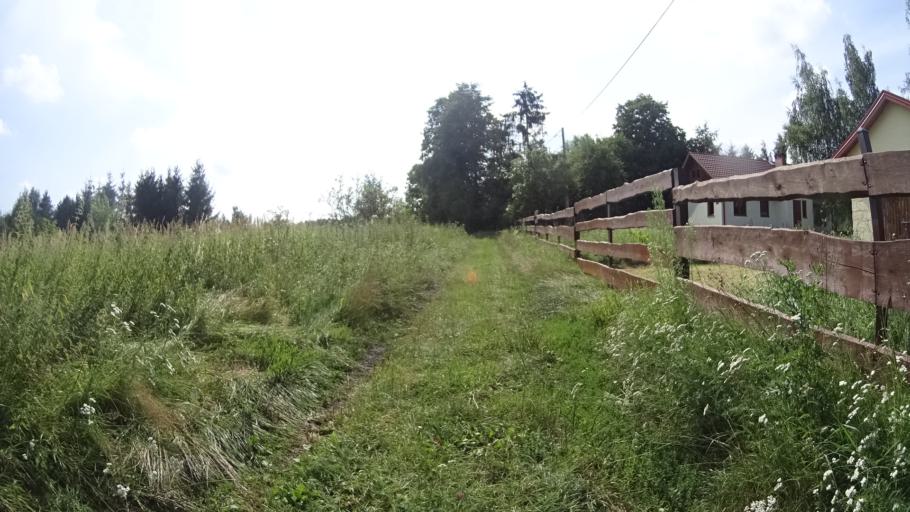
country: PL
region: Masovian Voivodeship
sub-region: Powiat grojecki
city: Goszczyn
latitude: 51.6940
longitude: 20.8356
